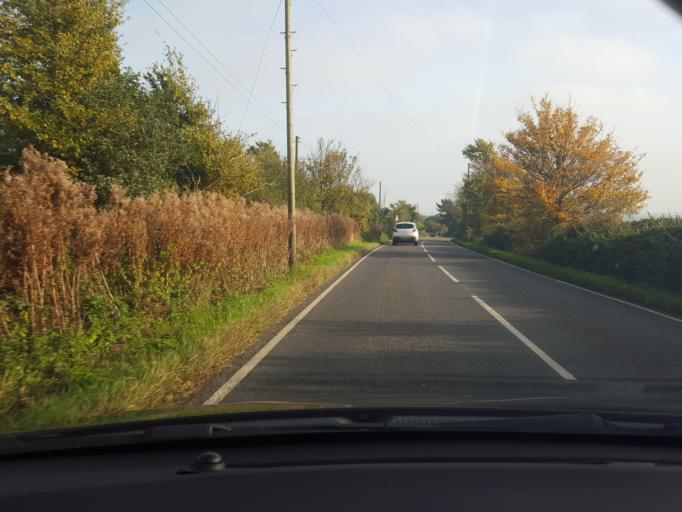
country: GB
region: England
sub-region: Essex
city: Little Clacton
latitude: 51.8933
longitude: 1.1887
